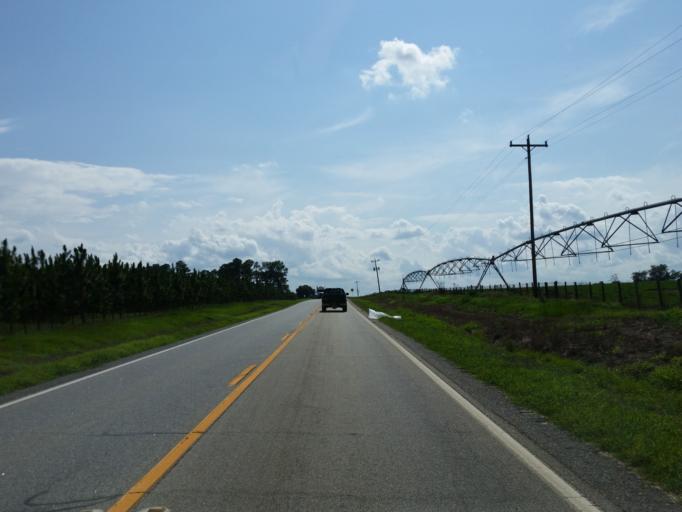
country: US
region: Georgia
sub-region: Turner County
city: Ashburn
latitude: 31.6774
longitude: -83.7524
